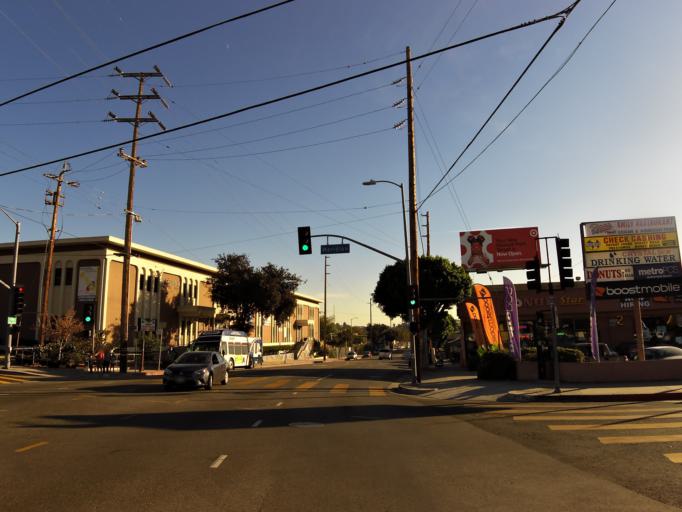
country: US
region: California
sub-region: Los Angeles County
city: South Pasadena
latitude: 34.1203
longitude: -118.1839
